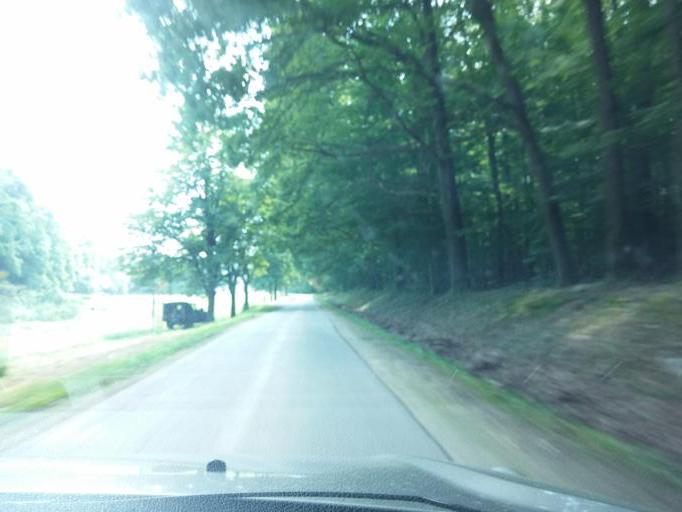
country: HU
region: Somogy
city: Kaposvar
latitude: 46.2489
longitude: 17.7775
